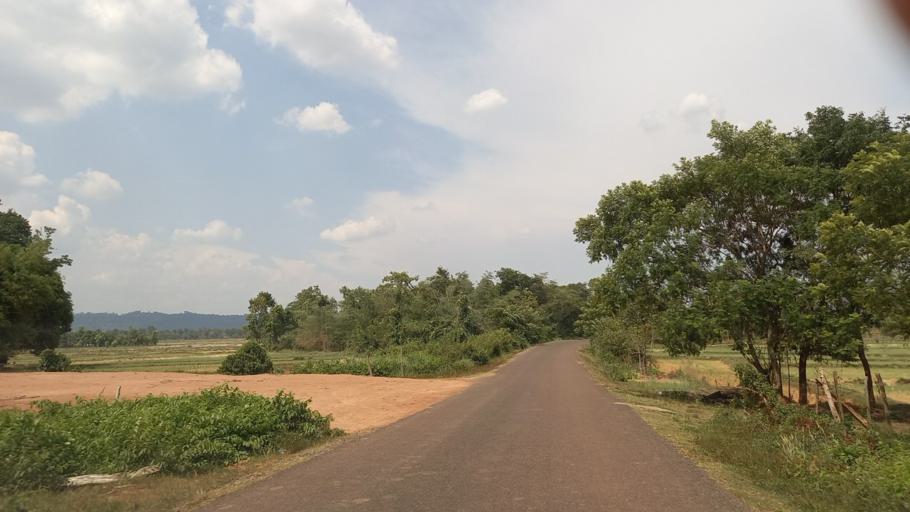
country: LA
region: Bolikhamxai
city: Muang Pakxan
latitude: 18.4290
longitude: 103.7204
